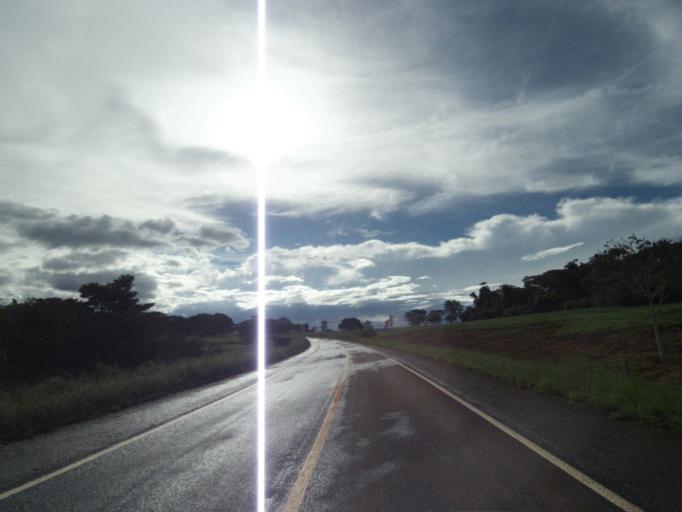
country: BR
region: Goias
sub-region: Itaberai
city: Itaberai
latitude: -15.9076
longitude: -49.5684
